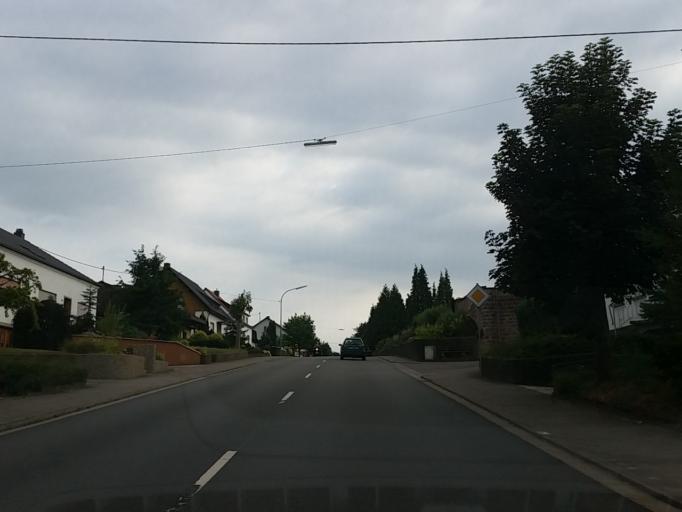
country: DE
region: Saarland
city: Schmelz
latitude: 49.4828
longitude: 6.8394
